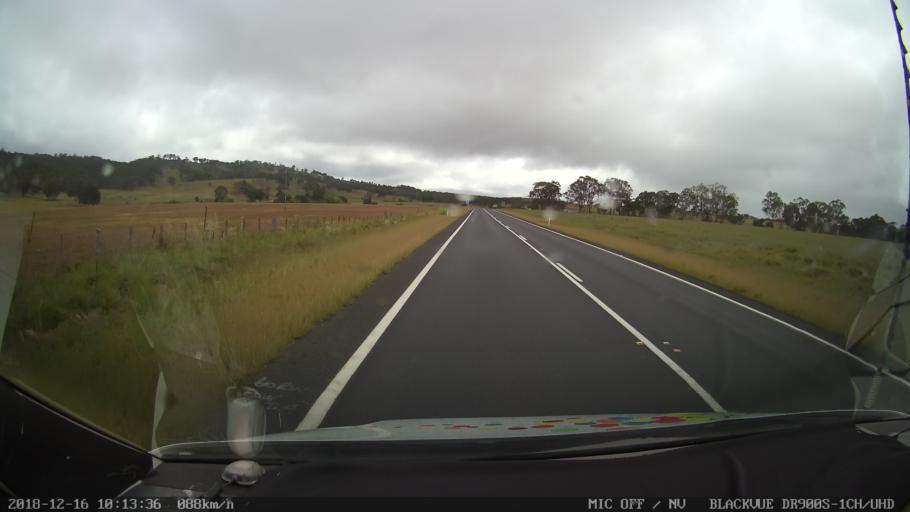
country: AU
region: New South Wales
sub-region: Glen Innes Severn
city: Glen Innes
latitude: -29.2959
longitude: 151.9542
